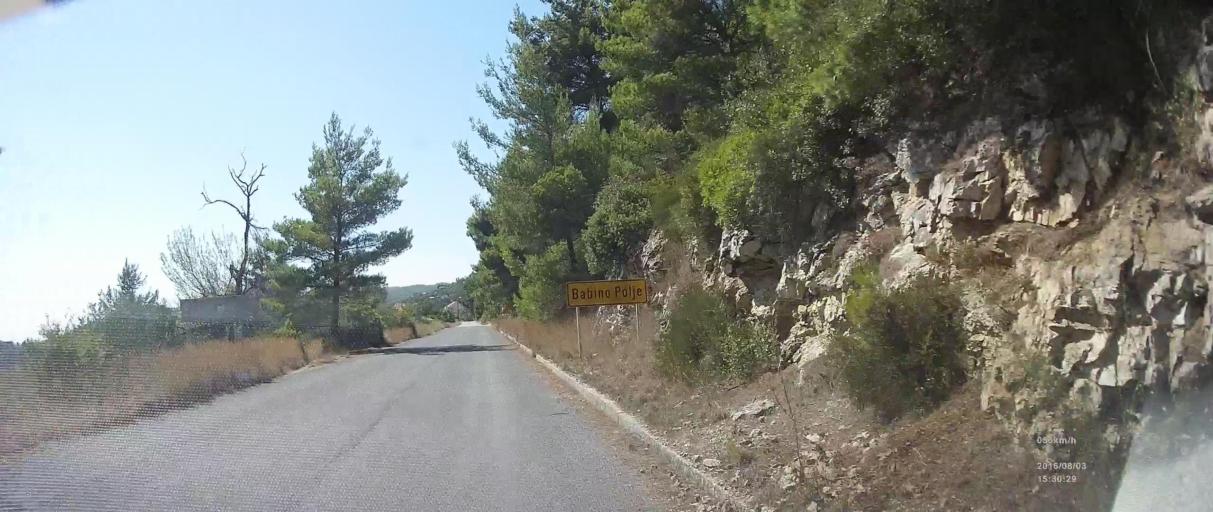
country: HR
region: Dubrovacko-Neretvanska
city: Blato
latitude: 42.7314
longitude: 17.5670
